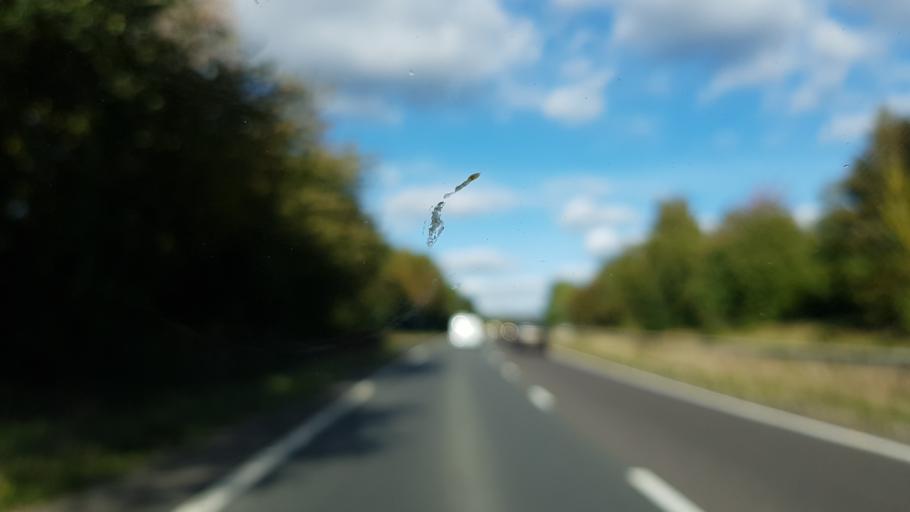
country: GB
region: England
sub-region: Surrey
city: Milford
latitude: 51.2117
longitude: -0.6498
